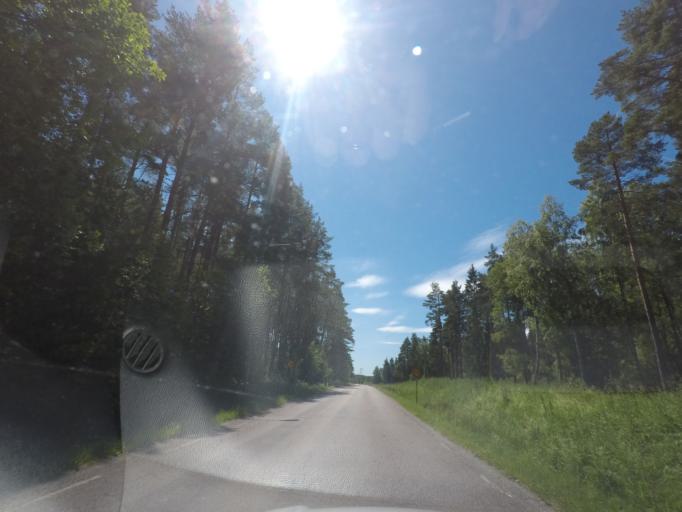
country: SE
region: Uppsala
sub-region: Enkopings Kommun
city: Irsta
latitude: 59.6734
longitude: 16.8381
